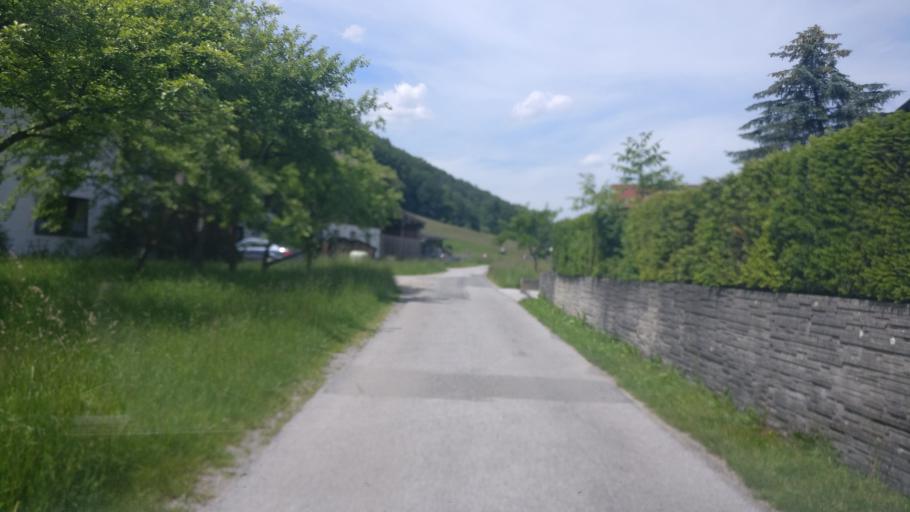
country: AT
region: Salzburg
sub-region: Politischer Bezirk Hallein
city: Adnet
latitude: 47.6531
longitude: 13.1201
